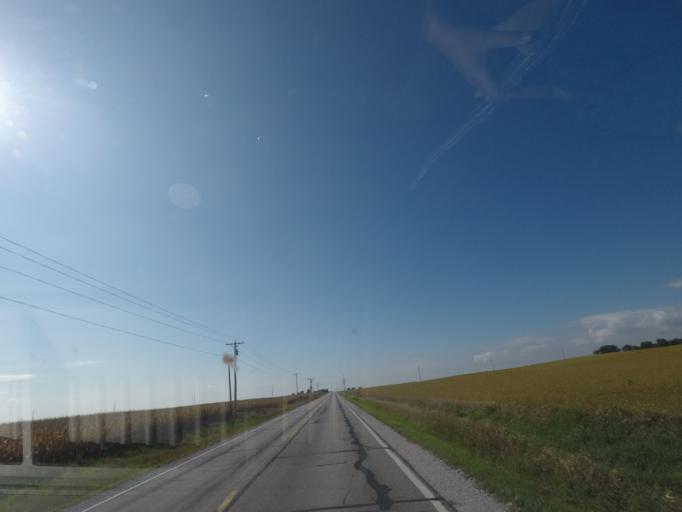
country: US
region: Iowa
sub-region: Story County
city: Nevada
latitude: 42.0381
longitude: -93.4058
